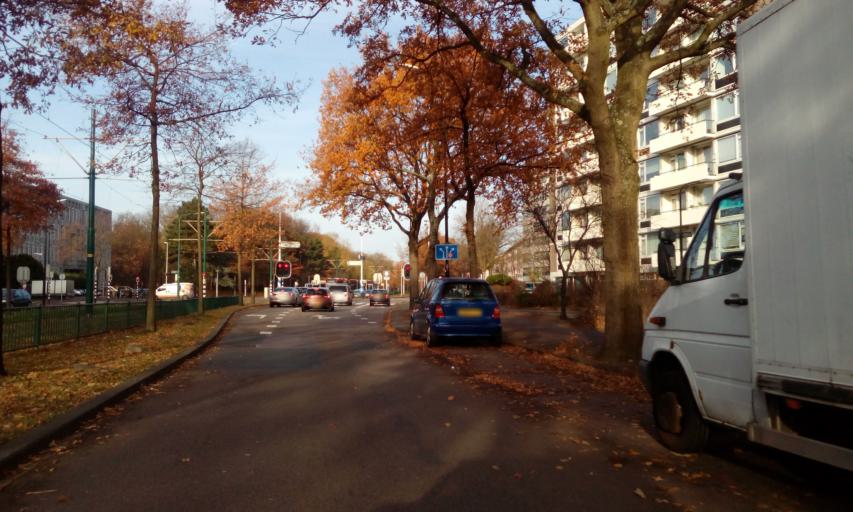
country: NL
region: South Holland
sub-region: Gemeente Rijswijk
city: Rijswijk
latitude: 52.0474
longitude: 4.3321
